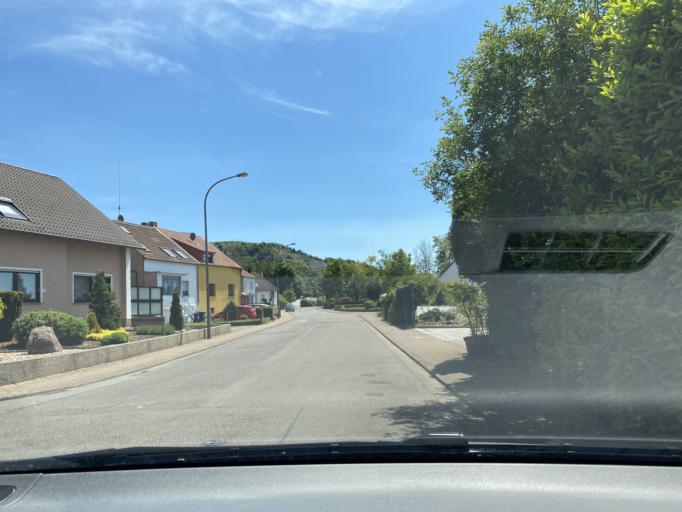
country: DE
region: Saarland
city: Saarlouis
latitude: 49.3240
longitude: 6.7725
